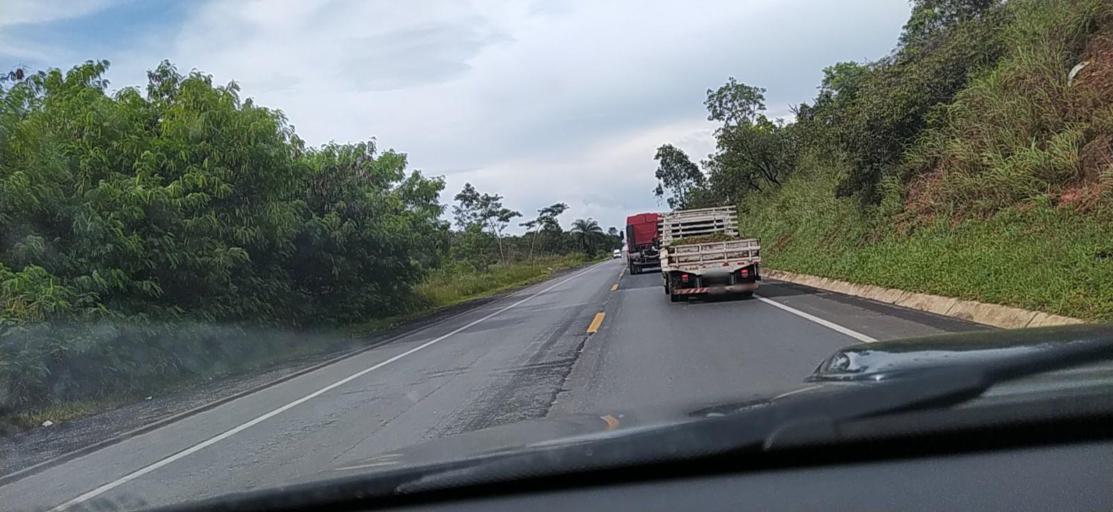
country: BR
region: Minas Gerais
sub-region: Montes Claros
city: Montes Claros
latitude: -16.8537
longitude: -43.8526
